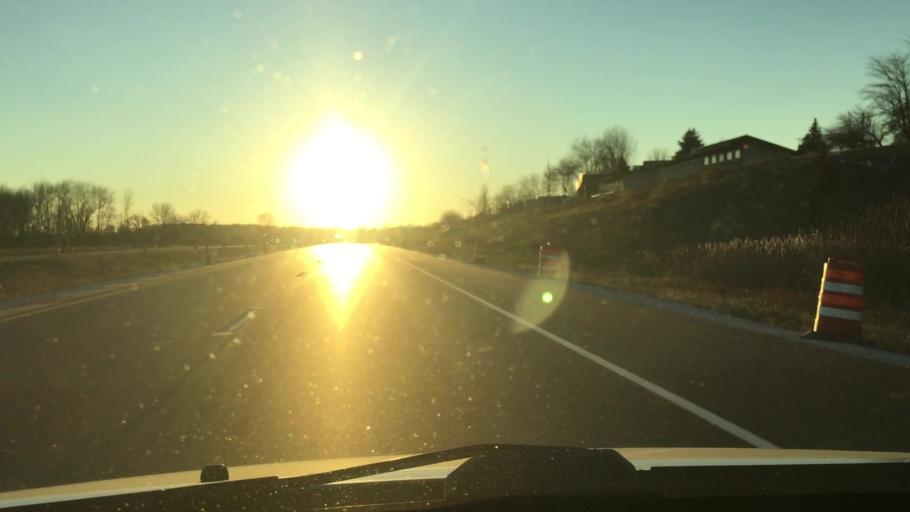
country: US
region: Wisconsin
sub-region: Waukesha County
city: Lannon
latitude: 43.0859
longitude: -88.1703
